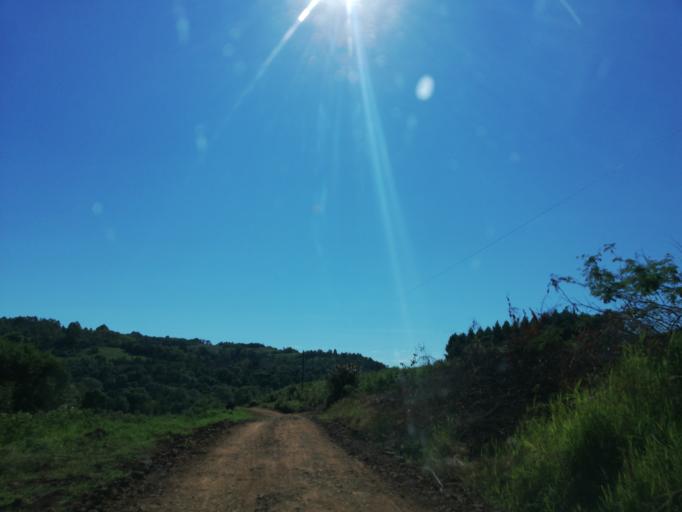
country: AR
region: Misiones
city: El Soberbio
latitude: -27.0676
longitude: -54.3872
